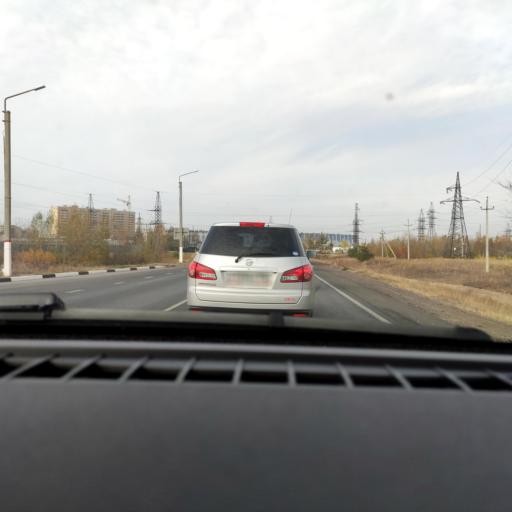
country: RU
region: Voronezj
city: Maslovka
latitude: 51.5870
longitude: 39.2546
